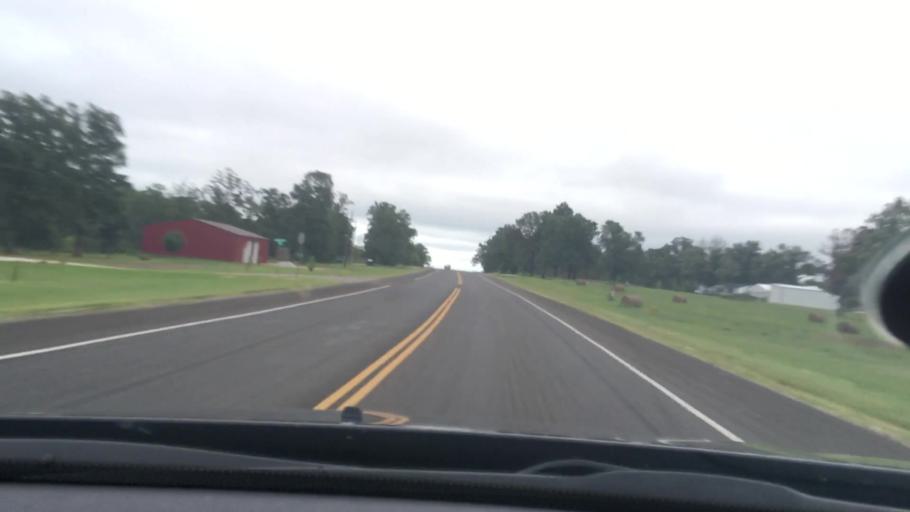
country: US
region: Oklahoma
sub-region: Sequoyah County
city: Vian
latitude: 35.5554
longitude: -94.9773
